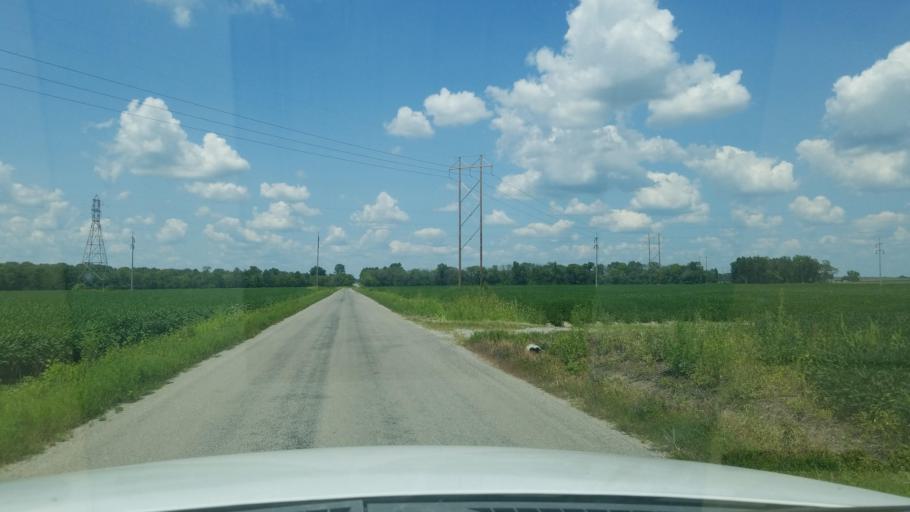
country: US
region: Illinois
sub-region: Saline County
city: Harrisburg
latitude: 37.7738
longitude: -88.5171
